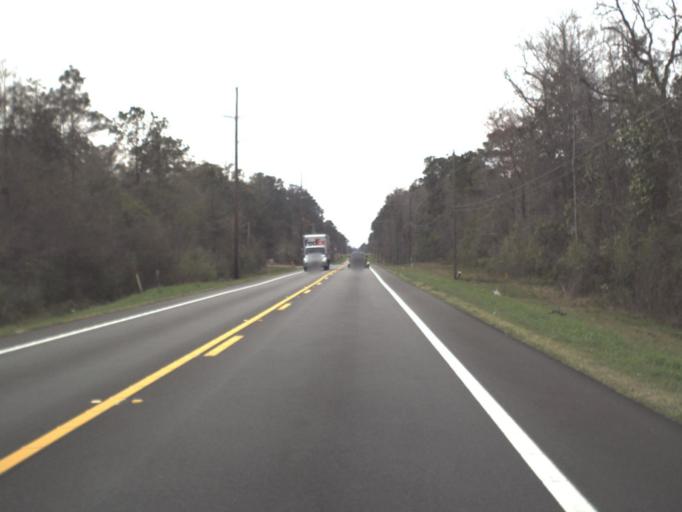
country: US
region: Florida
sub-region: Gadsden County
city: Midway
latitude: 30.3993
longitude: -84.5984
